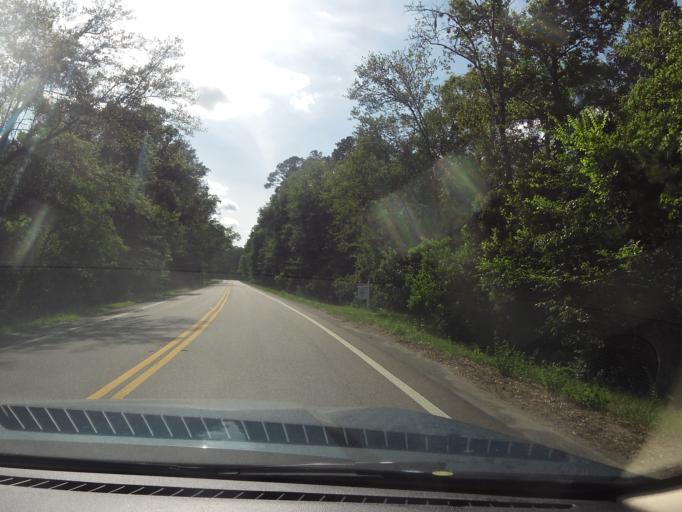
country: US
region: Florida
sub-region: Nassau County
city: Callahan
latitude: 30.5614
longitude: -81.8415
